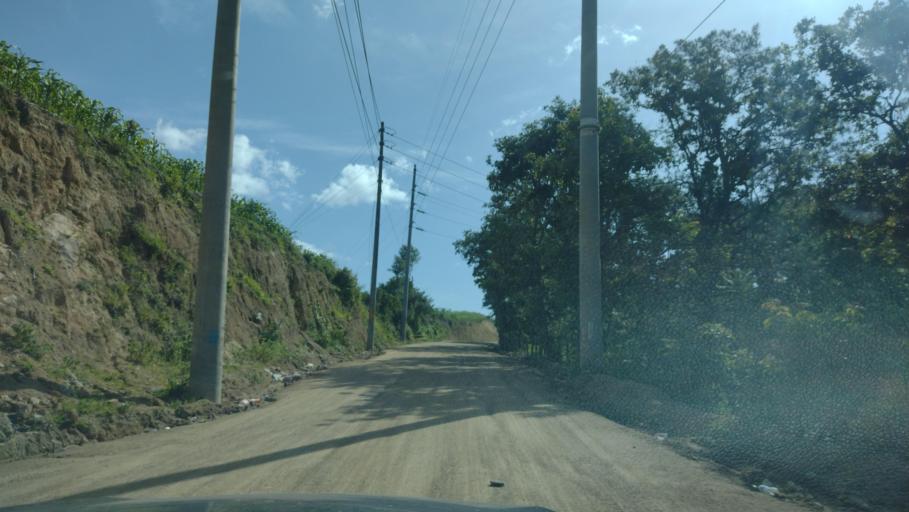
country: GT
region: Guatemala
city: Chinautla
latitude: 14.7532
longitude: -90.5132
